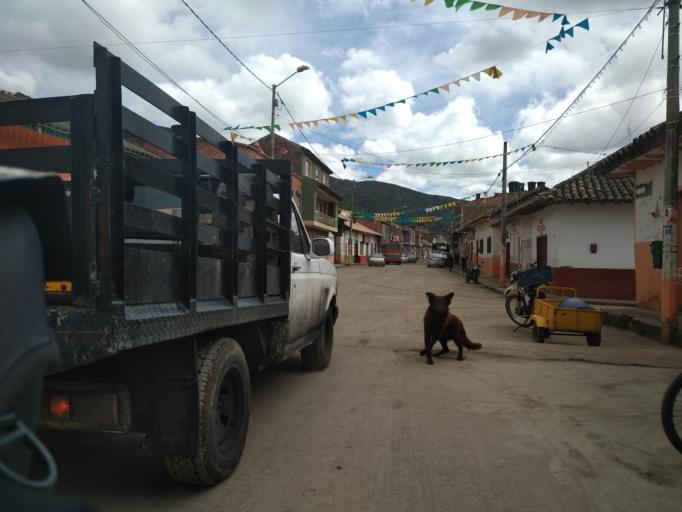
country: CO
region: Cundinamarca
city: Lenguazaque
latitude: 5.3049
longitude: -73.7115
